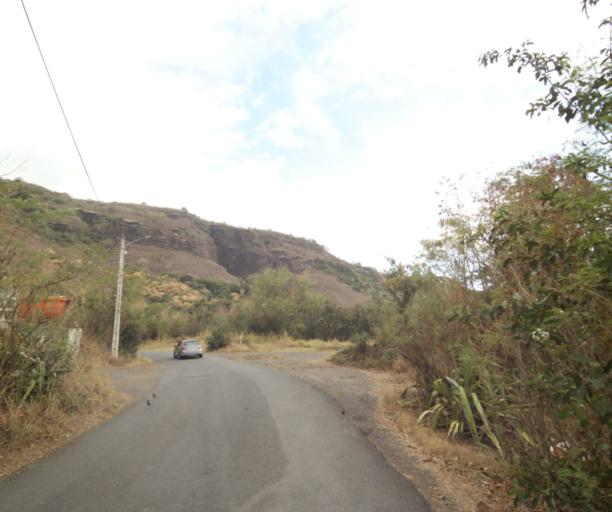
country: RE
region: Reunion
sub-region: Reunion
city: Saint-Paul
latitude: -21.0032
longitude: 55.2997
